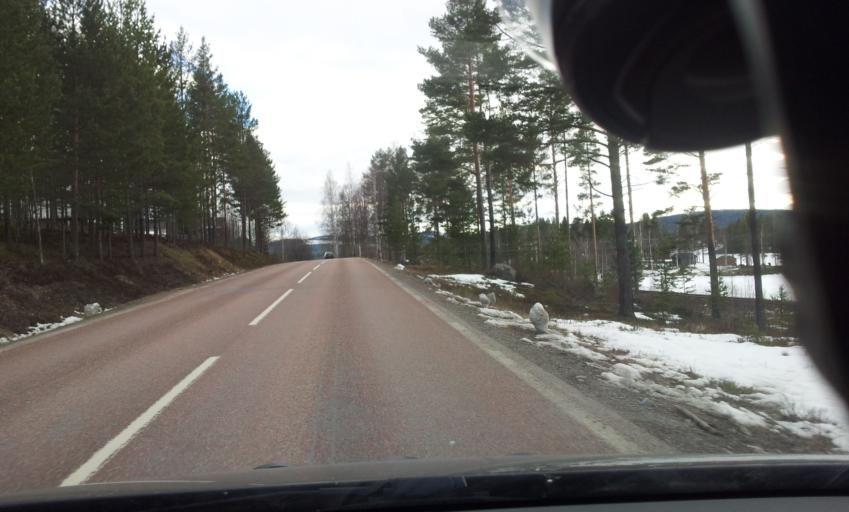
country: SE
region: Vaesternorrland
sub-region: Ange Kommun
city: Ange
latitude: 62.1576
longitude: 15.6769
